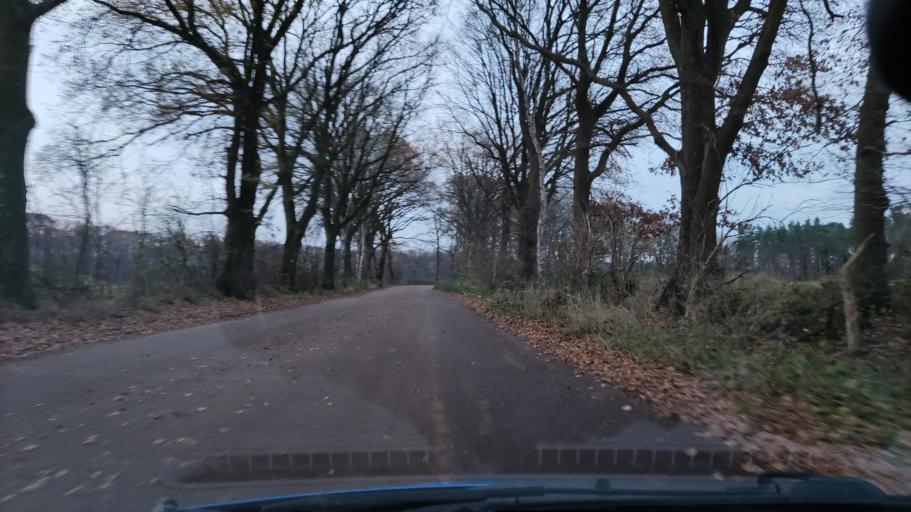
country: DE
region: Lower Saxony
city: Vogelsen
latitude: 53.2676
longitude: 10.3536
